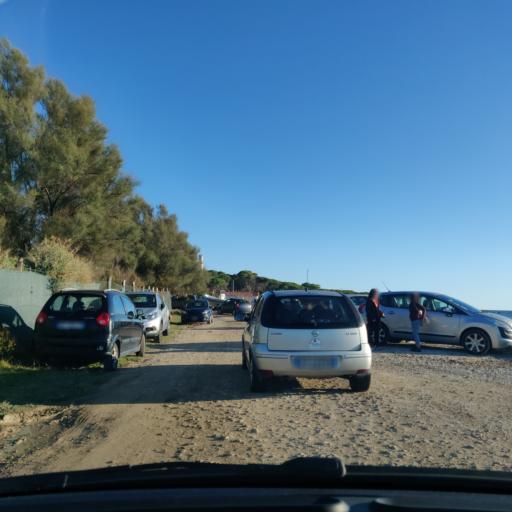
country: IT
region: Latium
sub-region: Citta metropolitana di Roma Capitale
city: Aurelia
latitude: 42.1488
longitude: 11.7440
